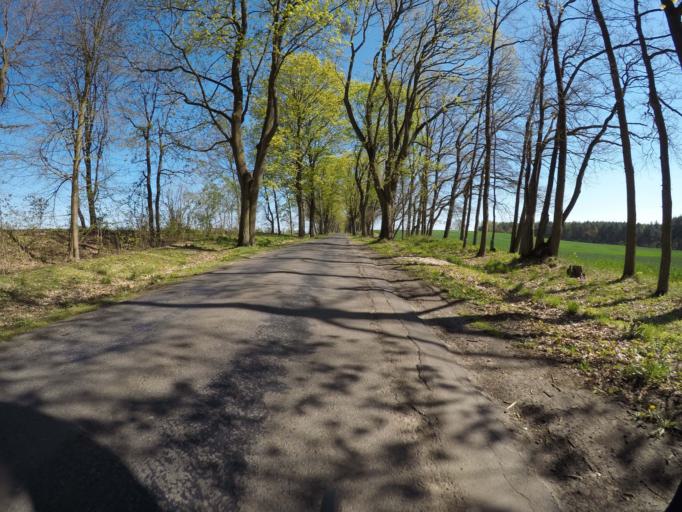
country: DE
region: Brandenburg
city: Strausberg
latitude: 52.6193
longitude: 13.8433
